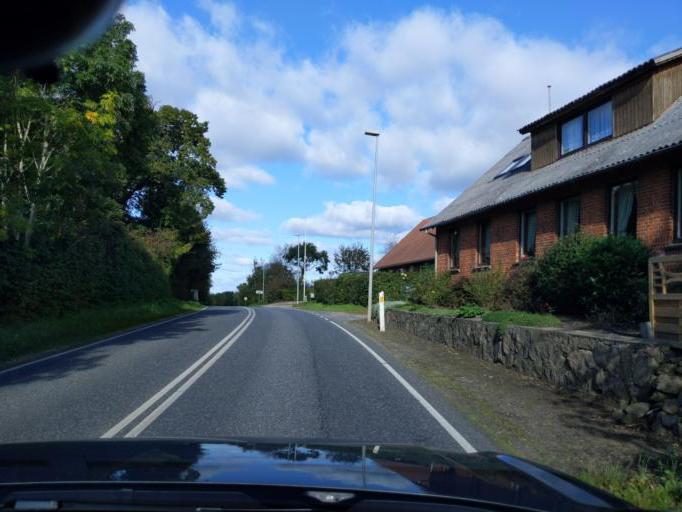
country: DK
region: Central Jutland
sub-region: Viborg Kommune
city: Bjerringbro
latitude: 56.4980
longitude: 9.5836
